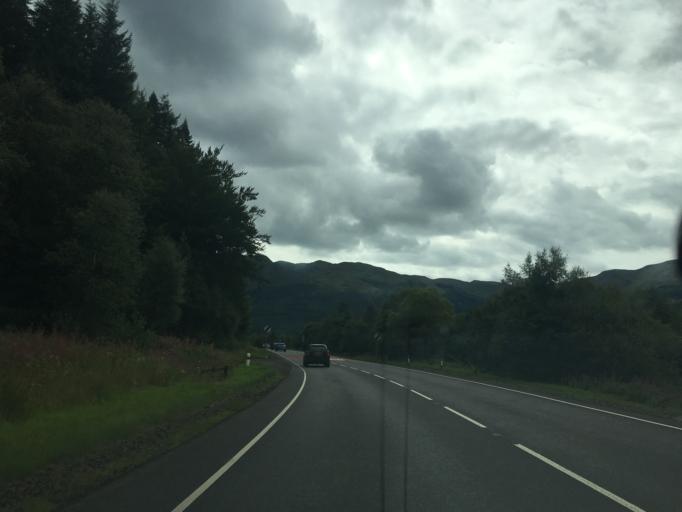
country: GB
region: Scotland
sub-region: Stirling
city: Callander
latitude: 56.3167
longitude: -4.3294
